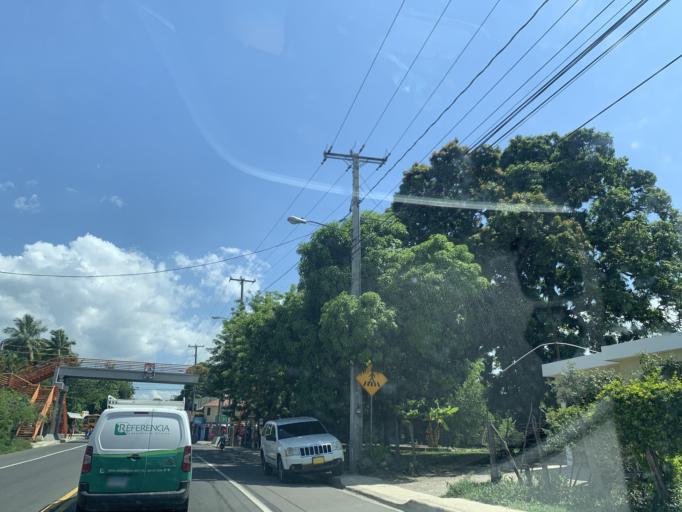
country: DO
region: Puerto Plata
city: Imbert
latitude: 19.7219
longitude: -70.8332
